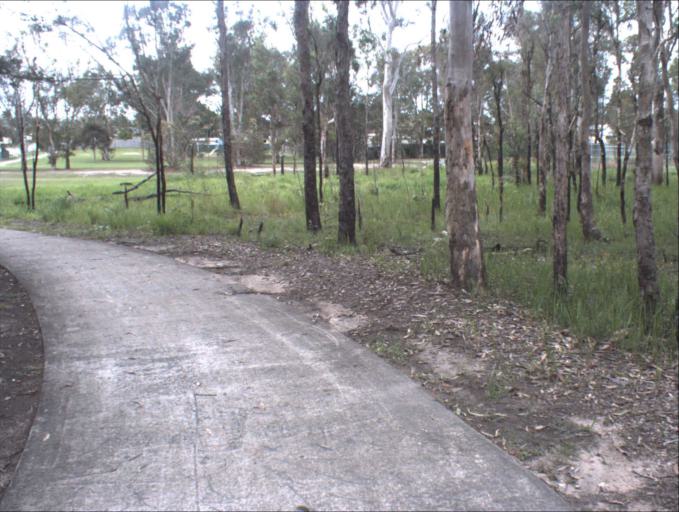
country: AU
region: Queensland
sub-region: Logan
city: Logan Reserve
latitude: -27.6922
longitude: 153.0873
